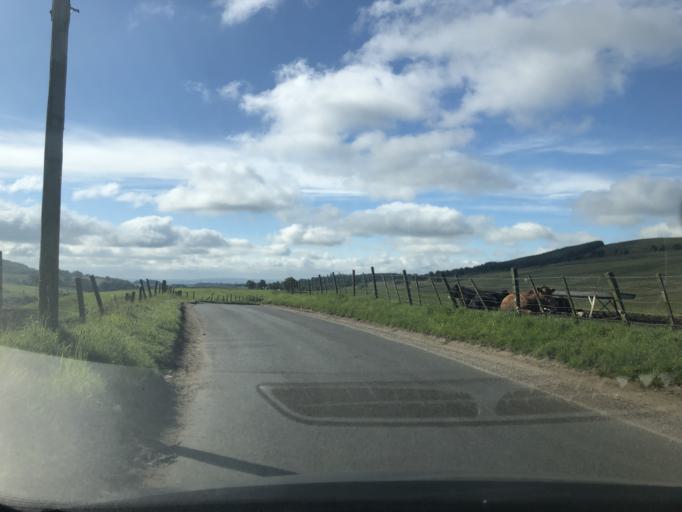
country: GB
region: Scotland
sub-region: Angus
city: Kirriemuir
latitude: 56.7608
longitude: -3.0194
